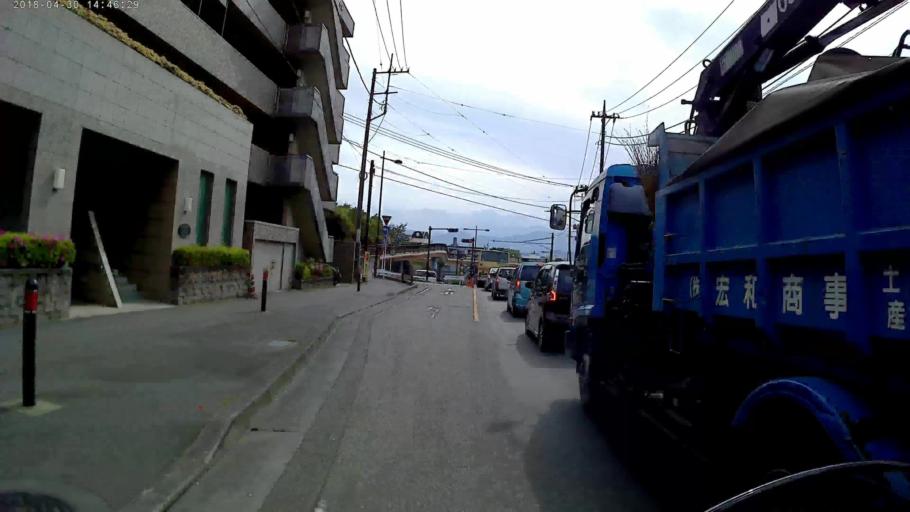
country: JP
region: Kanagawa
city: Zama
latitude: 35.5586
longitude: 139.3646
